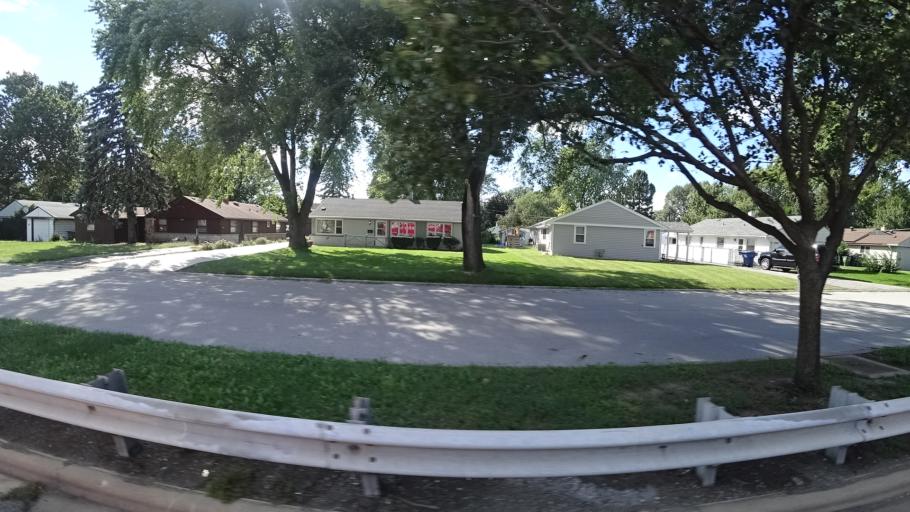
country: US
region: Illinois
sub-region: Cook County
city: Oak Lawn
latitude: 41.7096
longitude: -87.7405
